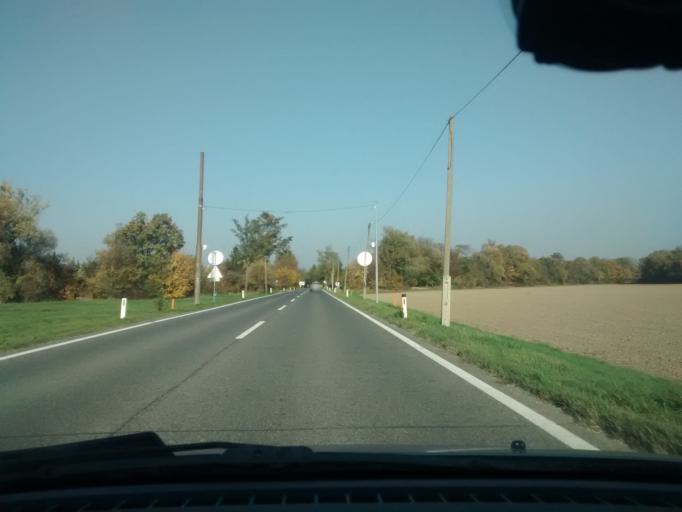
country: AT
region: Lower Austria
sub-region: Politischer Bezirk Modling
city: Achau
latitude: 48.0775
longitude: 16.3890
